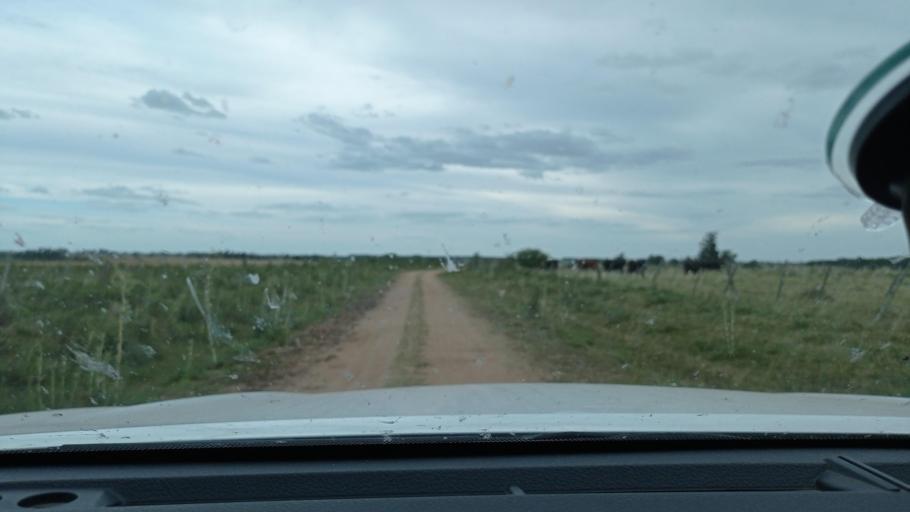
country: UY
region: Florida
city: Casupa
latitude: -34.1308
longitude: -55.8013
